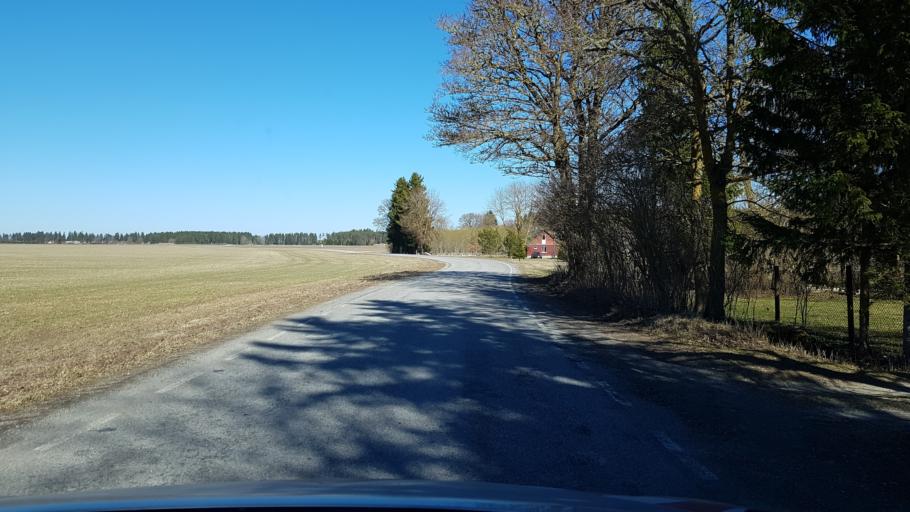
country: EE
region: Laeaene-Virumaa
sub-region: Someru vald
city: Someru
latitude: 59.3979
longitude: 26.5070
